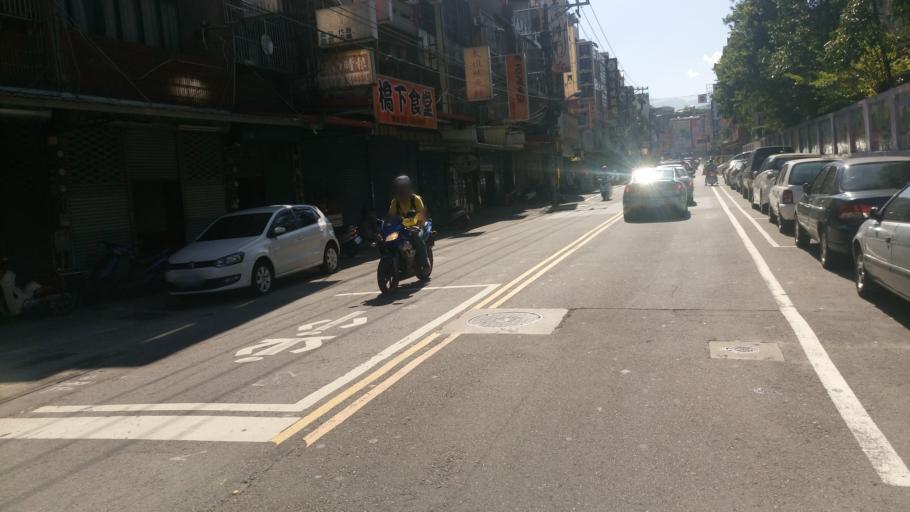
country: TW
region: Taiwan
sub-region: Hsinchu
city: Zhubei
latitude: 24.7356
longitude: 121.0886
